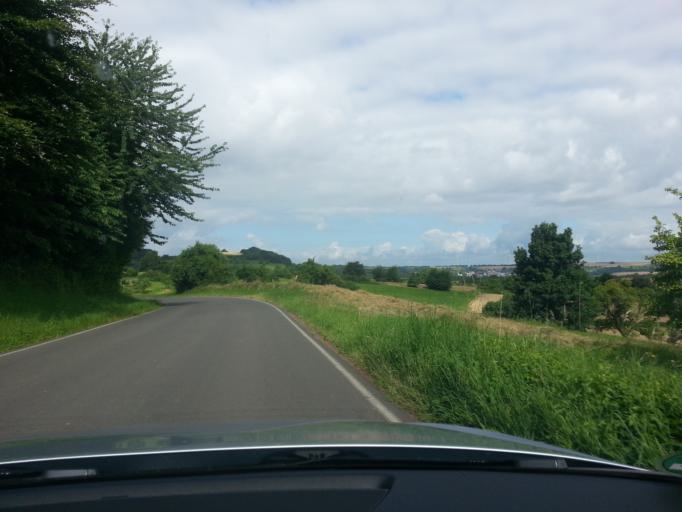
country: DE
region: Saarland
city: Orscholz
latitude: 49.5251
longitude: 6.5092
